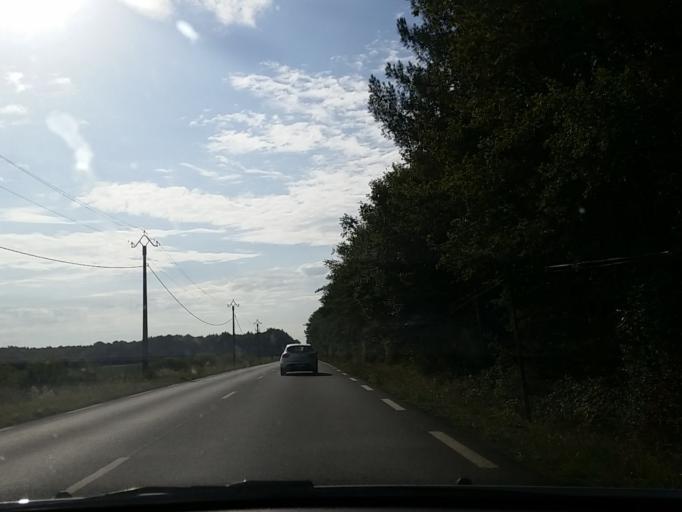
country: FR
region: Centre
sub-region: Departement du Loir-et-Cher
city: Mur-de-Sologne
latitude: 47.4238
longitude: 1.5811
